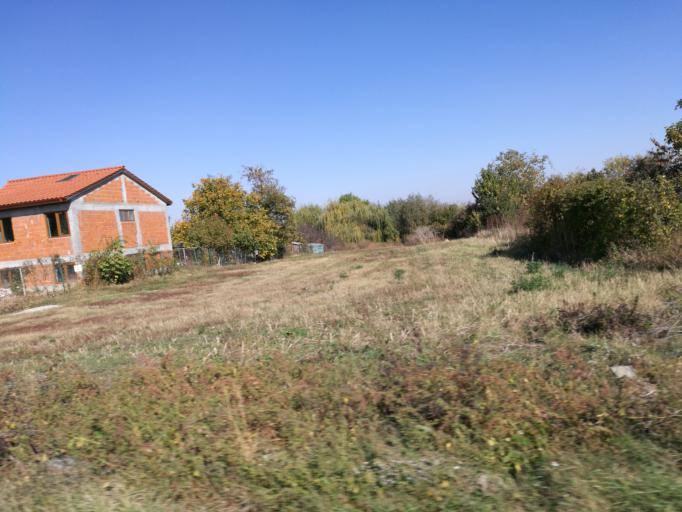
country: RO
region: Ilfov
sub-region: Comuna Dragomiresti-Vale
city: Dragomiresti-Vale
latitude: 44.4653
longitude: 25.9299
